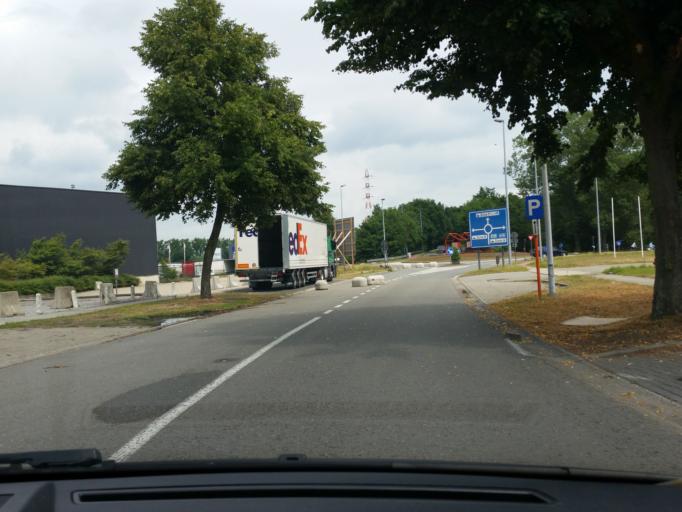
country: BE
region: Flanders
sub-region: Provincie Antwerpen
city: Rumst
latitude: 51.0524
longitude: 4.4469
